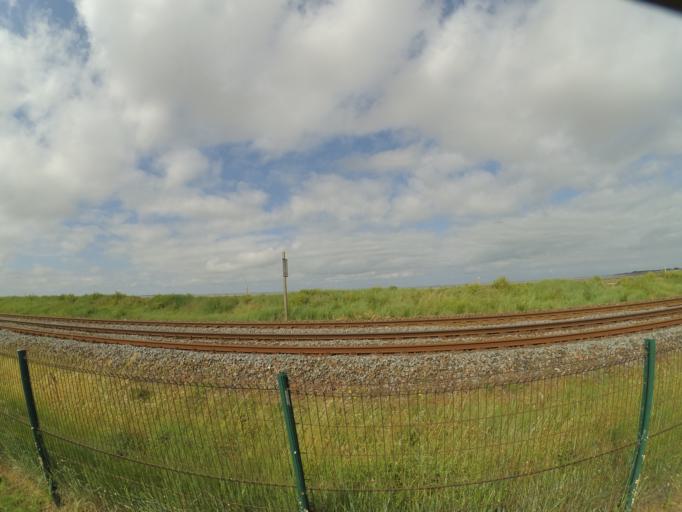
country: FR
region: Poitou-Charentes
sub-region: Departement de la Charente-Maritime
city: Angoulins
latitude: 46.0899
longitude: -1.0987
